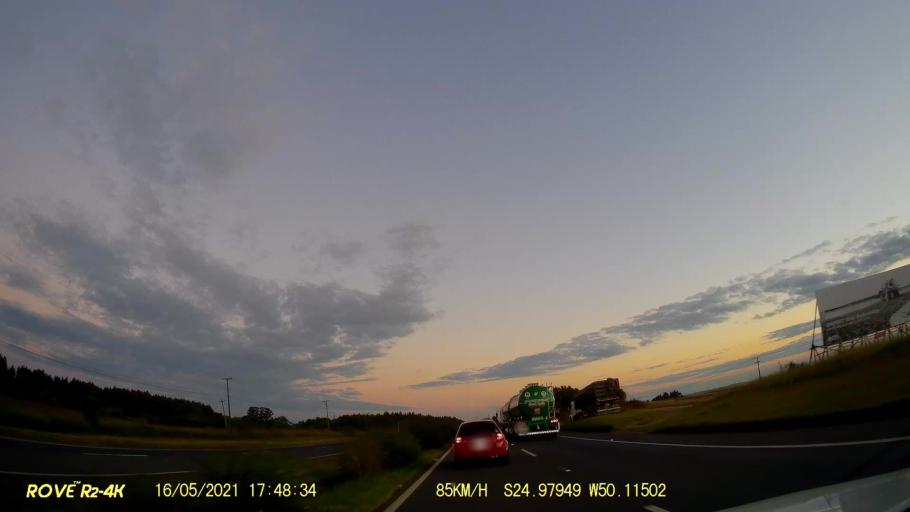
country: BR
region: Parana
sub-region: Carambei
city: Carambei
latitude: -24.9791
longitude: -50.1168
